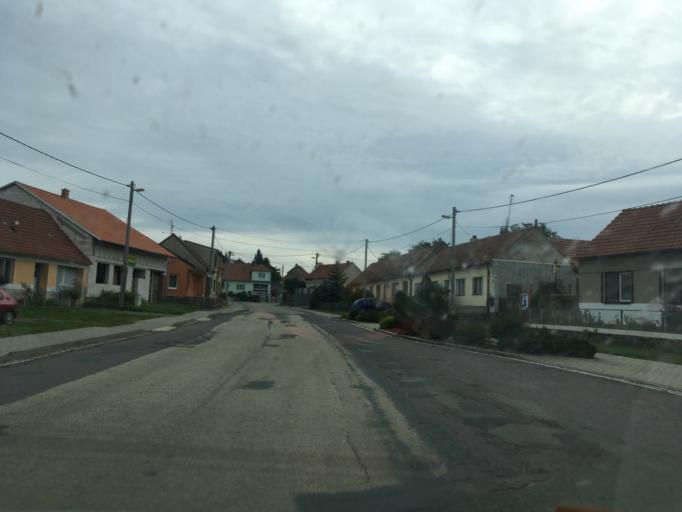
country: CZ
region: South Moravian
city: Zbraslav
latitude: 49.1590
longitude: 16.2644
